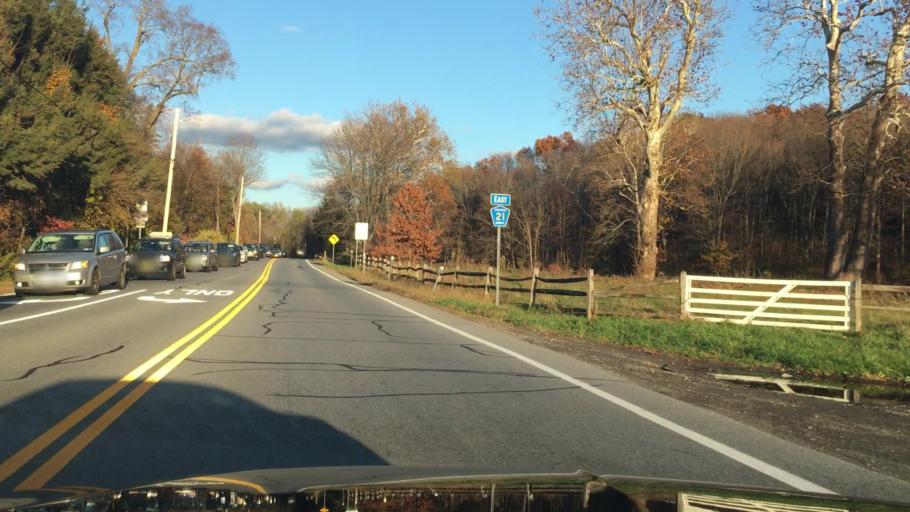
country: US
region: New York
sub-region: Dutchess County
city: Hillside Lake
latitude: 41.6419
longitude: -73.7939
